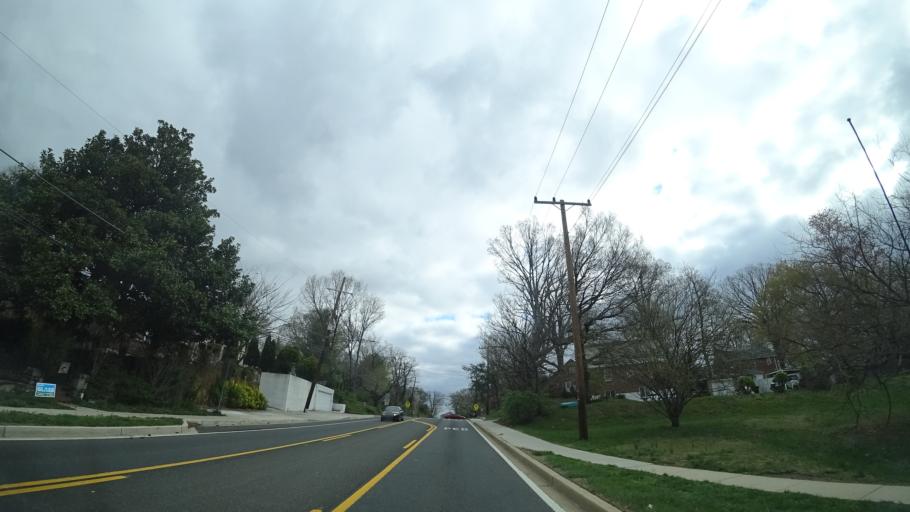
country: US
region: Maryland
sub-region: Montgomery County
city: Takoma Park
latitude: 38.9873
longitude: -77.0129
